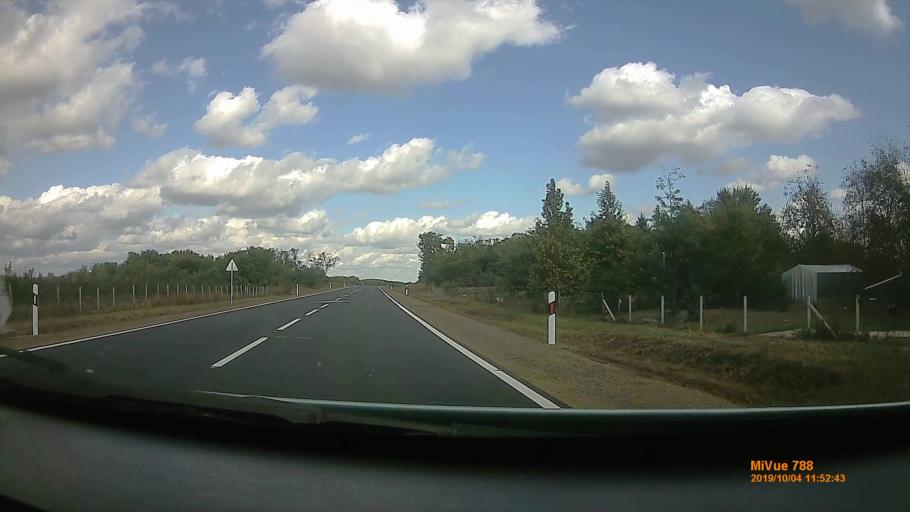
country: HU
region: Szabolcs-Szatmar-Bereg
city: Nyirtelek
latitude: 48.0016
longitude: 21.6729
